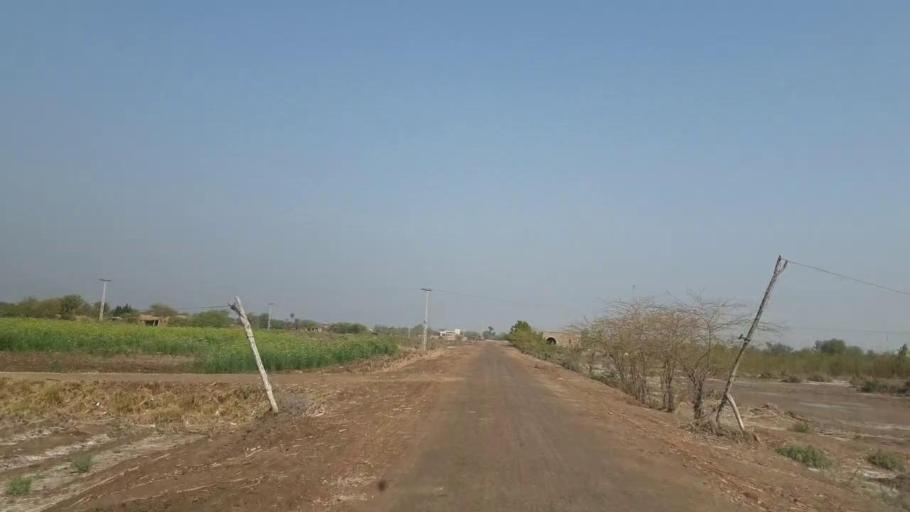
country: PK
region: Sindh
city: Mirpur Khas
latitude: 25.5934
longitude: 69.0148
